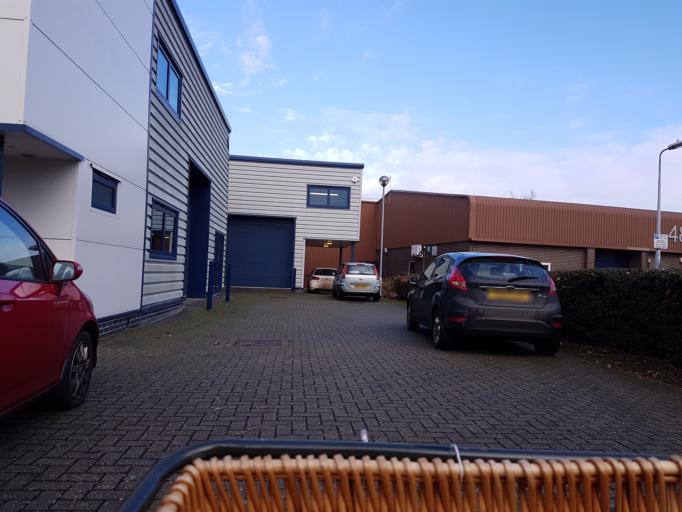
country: GB
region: England
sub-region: Cambridgeshire
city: Cambridge
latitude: 52.1931
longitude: 0.1386
